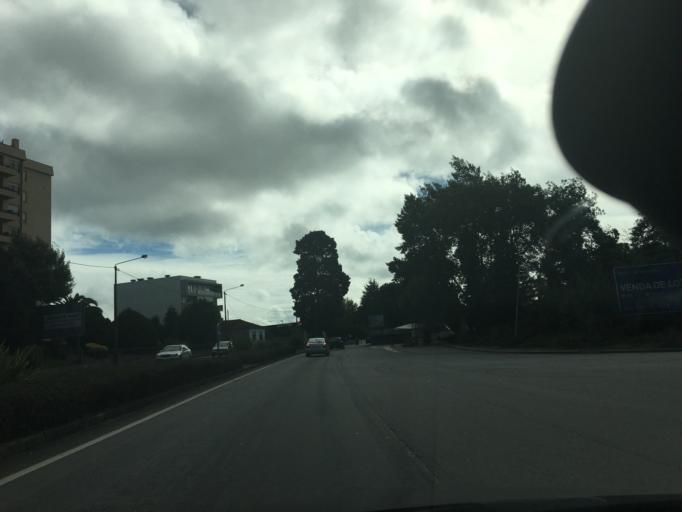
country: PT
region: Porto
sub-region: Maia
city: Gemunde
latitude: 41.2498
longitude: -8.6498
